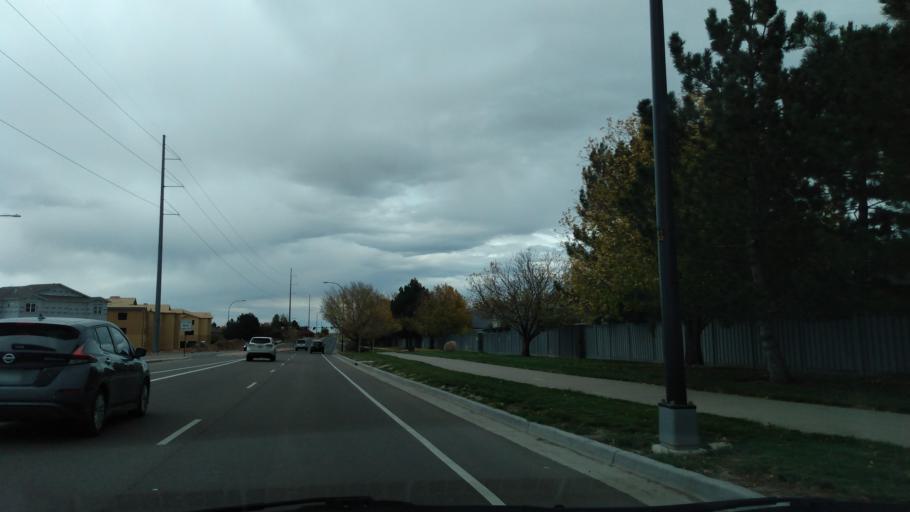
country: US
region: Colorado
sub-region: Adams County
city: Northglenn
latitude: 39.9294
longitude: -104.9779
